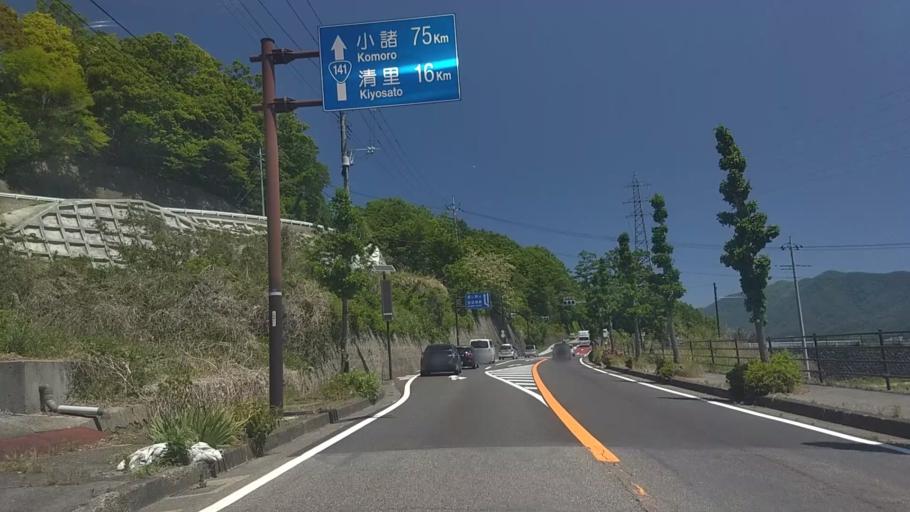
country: JP
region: Yamanashi
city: Nirasaki
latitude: 35.8005
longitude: 138.4252
